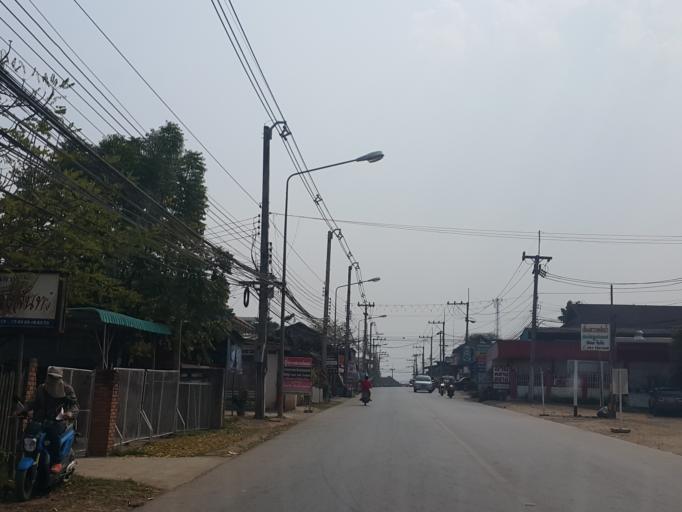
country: TH
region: Chiang Mai
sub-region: Amphoe Chiang Dao
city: Chiang Dao
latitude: 19.3741
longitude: 98.9664
